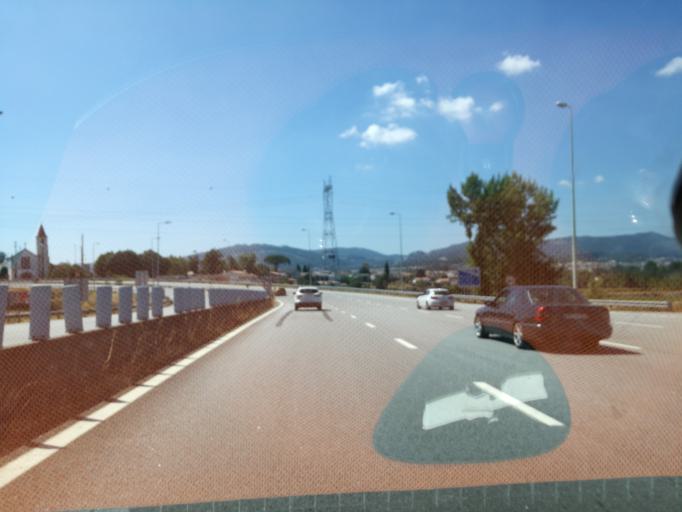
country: PT
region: Braga
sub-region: Guimaraes
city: Candoso
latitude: 41.4446
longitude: -8.3330
